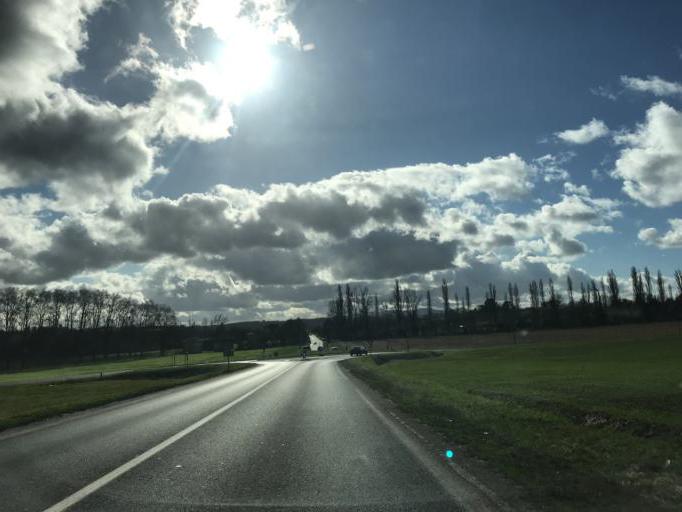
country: FR
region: Rhone-Alpes
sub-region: Departement de l'Ain
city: Sainte-Euphemie
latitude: 45.9828
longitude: 4.7974
